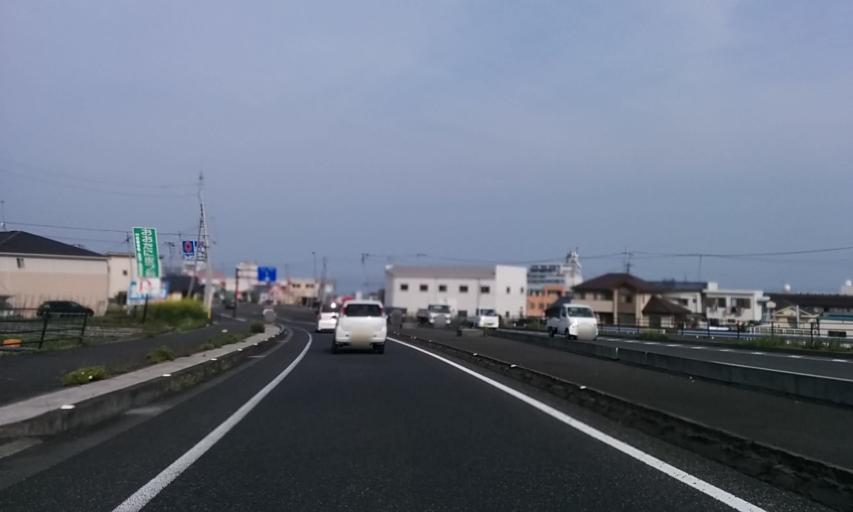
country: JP
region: Ehime
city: Kawanoecho
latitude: 33.9740
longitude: 133.5319
